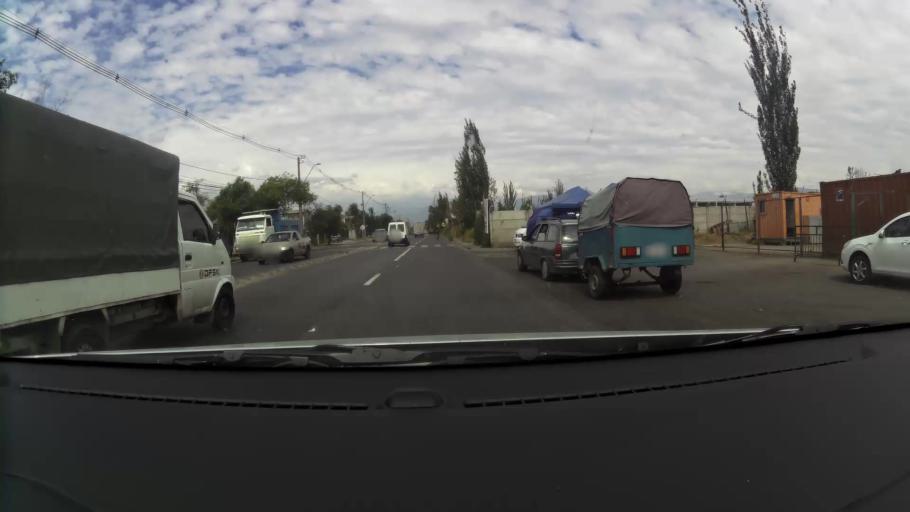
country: CL
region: Santiago Metropolitan
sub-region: Provincia de Santiago
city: La Pintana
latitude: -33.5857
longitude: -70.6599
